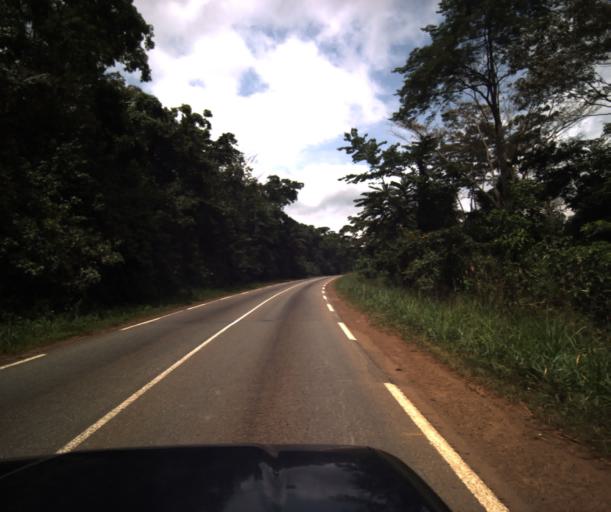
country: CM
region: Centre
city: Mbankomo
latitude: 3.7713
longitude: 11.1687
